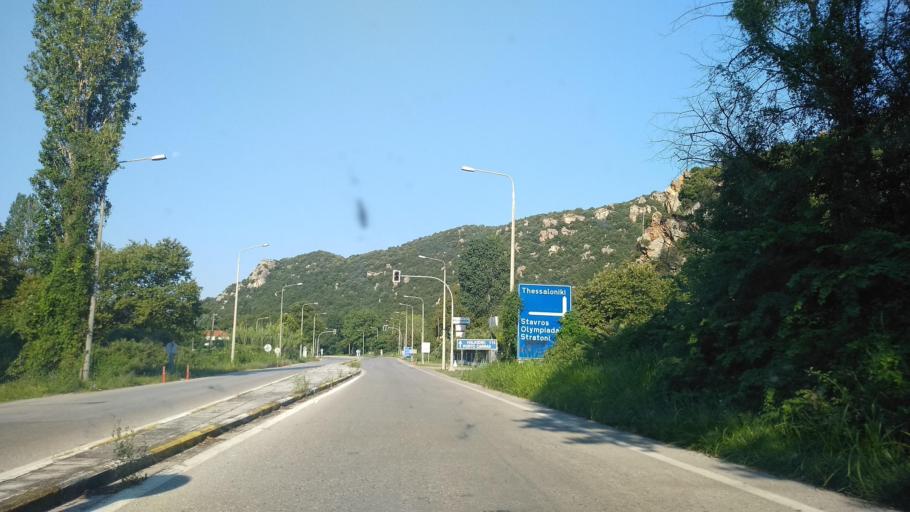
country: GR
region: Central Macedonia
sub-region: Nomos Thessalonikis
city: Stavros
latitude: 40.6730
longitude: 23.6652
